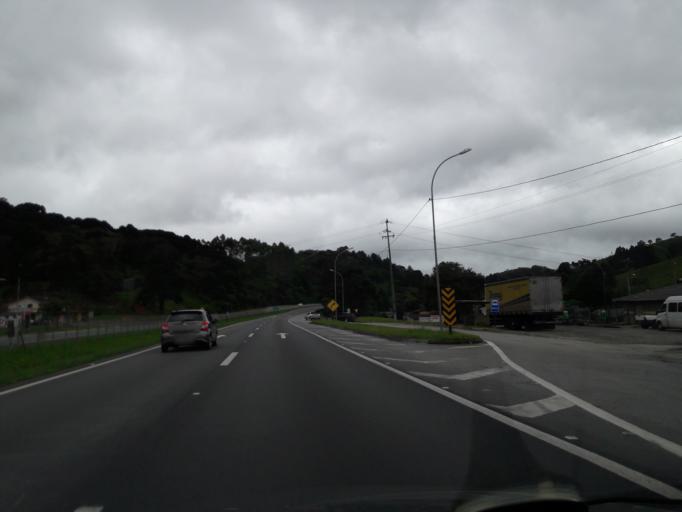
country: BR
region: Parana
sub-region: Campina Grande Do Sul
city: Campina Grande do Sul
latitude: -25.2181
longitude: -48.9042
